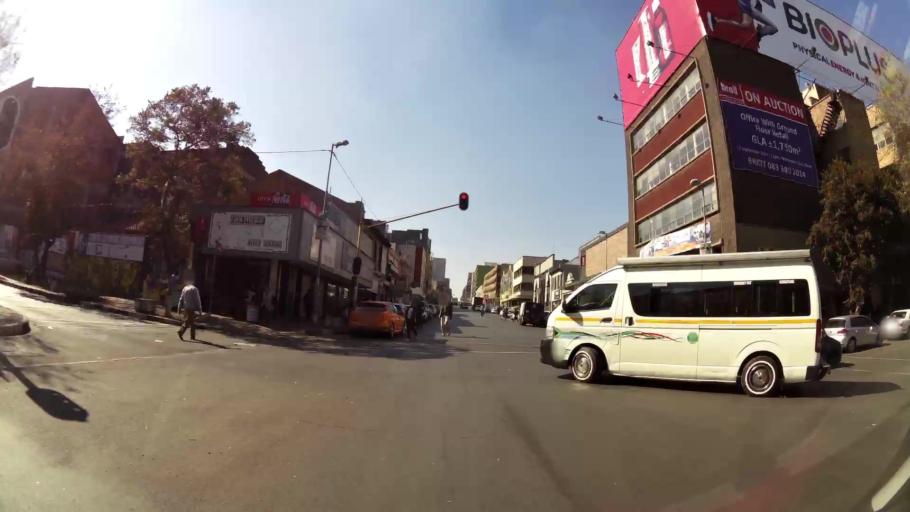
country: ZA
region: Gauteng
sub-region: City of Johannesburg Metropolitan Municipality
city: Johannesburg
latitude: -26.2018
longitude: 28.0331
